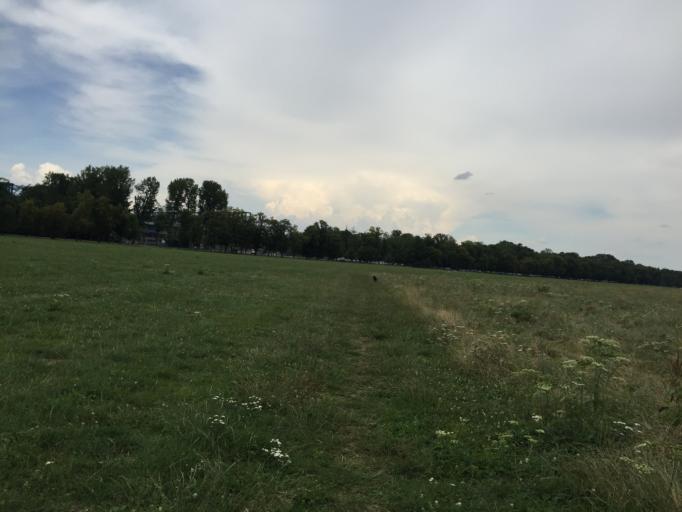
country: PL
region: Lesser Poland Voivodeship
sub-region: Krakow
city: Krakow
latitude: 50.0597
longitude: 19.9072
